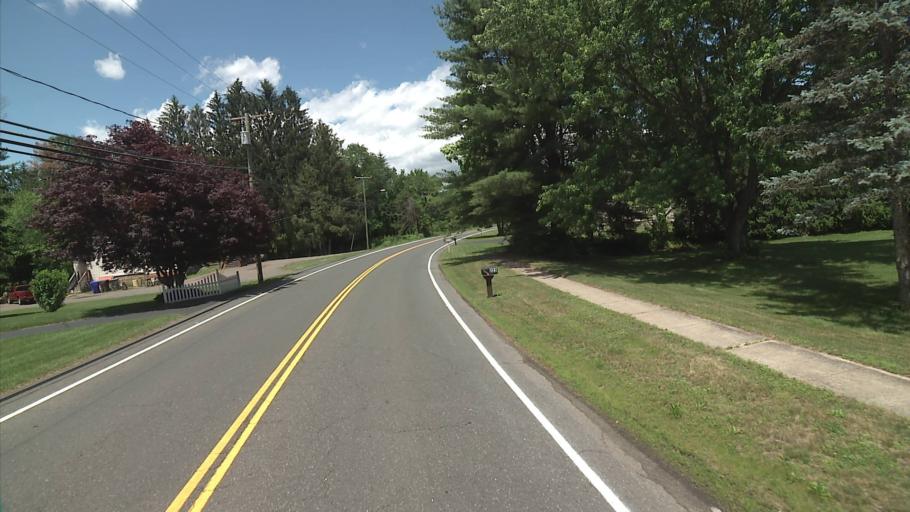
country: US
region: Connecticut
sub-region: Hartford County
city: Sherwood Manor
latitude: 42.0146
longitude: -72.5422
